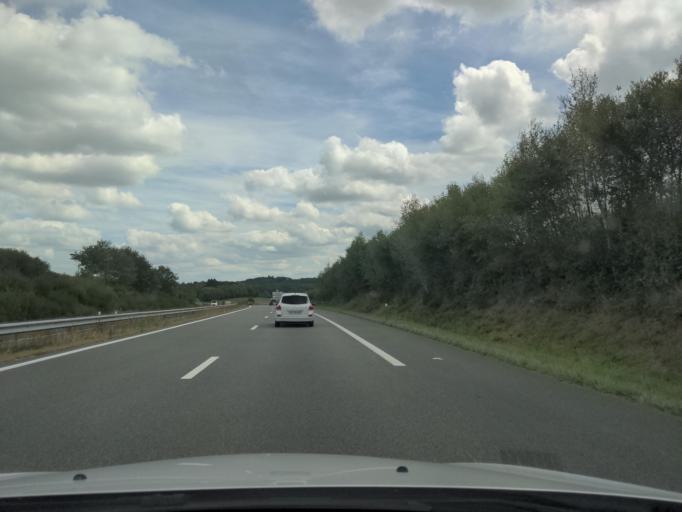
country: FR
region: Limousin
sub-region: Departement de la Creuse
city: Le Grand-Bourg
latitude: 46.2213
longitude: 1.5909
